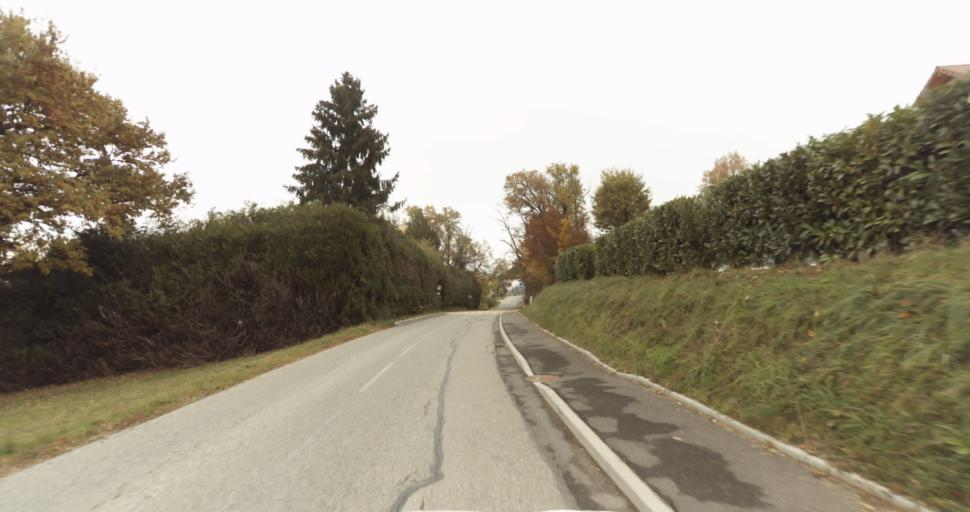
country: FR
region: Rhone-Alpes
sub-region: Departement de la Haute-Savoie
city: Saint-Felix
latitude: 45.7851
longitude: 5.9882
